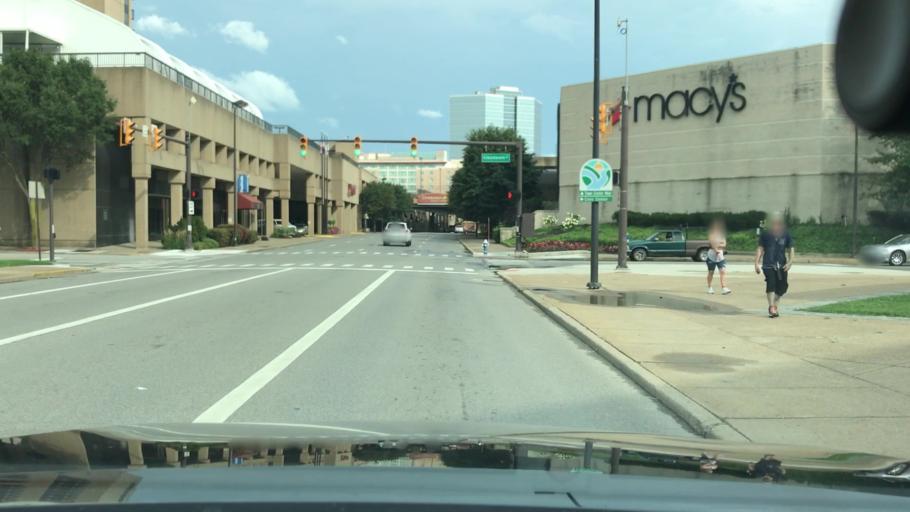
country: US
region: West Virginia
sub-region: Kanawha County
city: Charleston
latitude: 38.3561
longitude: -81.6390
